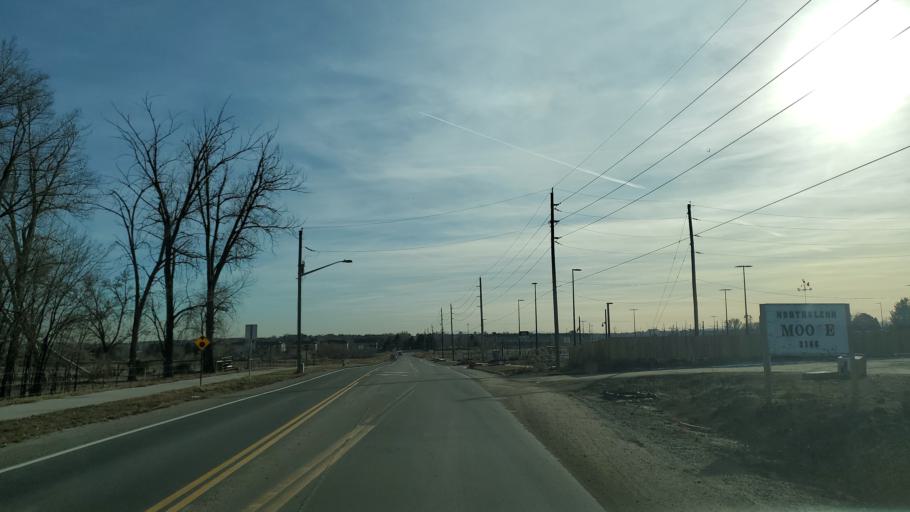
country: US
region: Colorado
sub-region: Adams County
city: Northglenn
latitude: 39.9038
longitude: -104.9589
